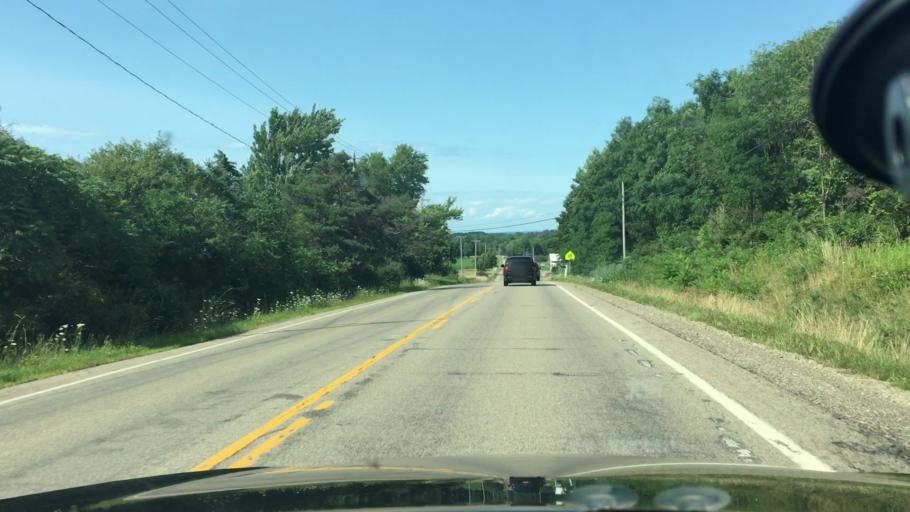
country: US
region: New York
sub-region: Chautauqua County
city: Fredonia
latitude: 42.4124
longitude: -79.3131
